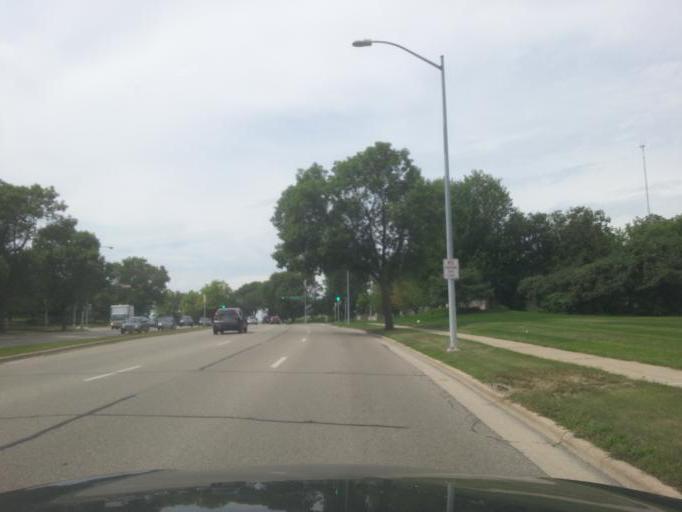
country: US
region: Wisconsin
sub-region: Dane County
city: Shorewood Hills
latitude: 43.0569
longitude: -89.4728
